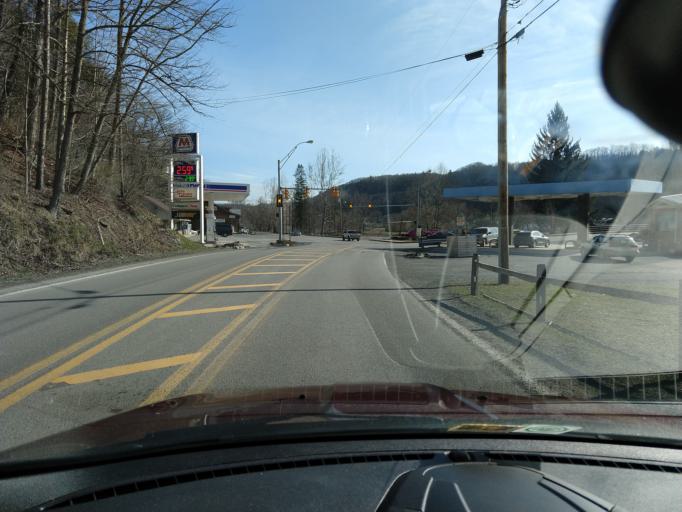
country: US
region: West Virginia
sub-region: Pocahontas County
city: Marlinton
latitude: 38.2248
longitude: -80.0974
